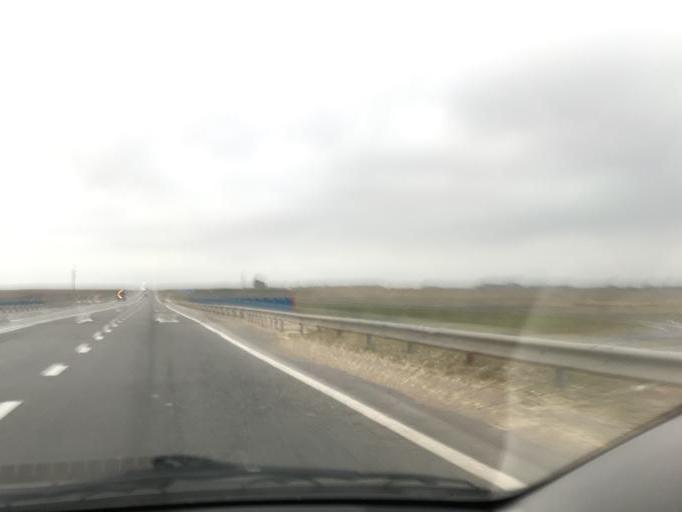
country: BY
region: Vitebsk
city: Vitebsk
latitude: 55.1563
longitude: 30.0654
